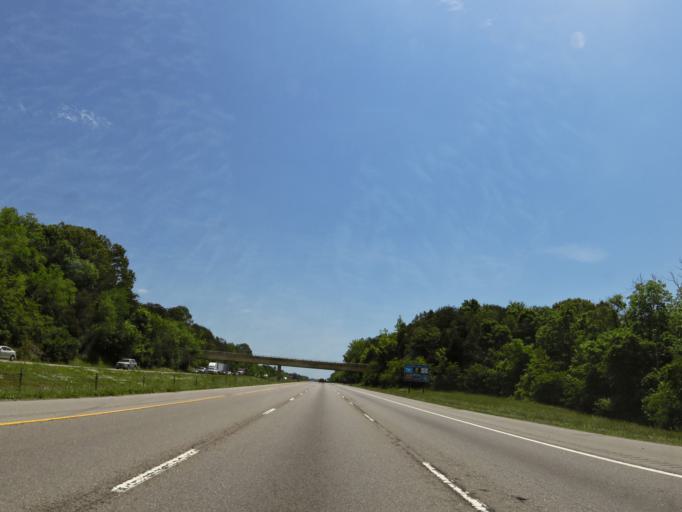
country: US
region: Tennessee
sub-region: Knox County
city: Mascot
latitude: 36.0065
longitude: -83.8079
